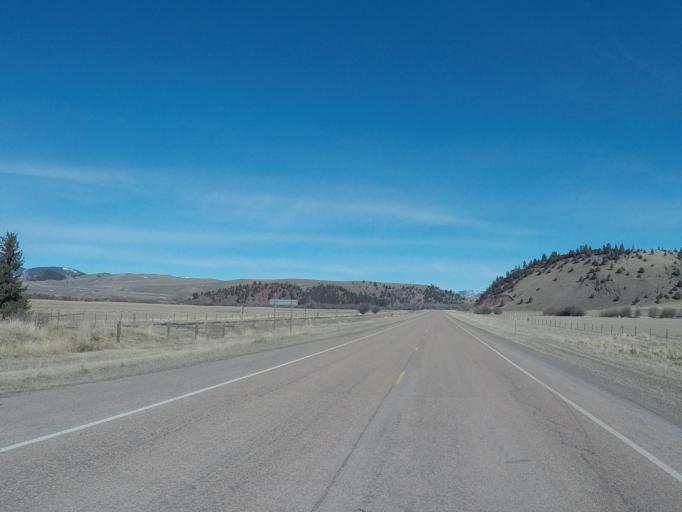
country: US
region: Montana
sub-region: Granite County
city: Philipsburg
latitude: 46.5053
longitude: -113.2249
